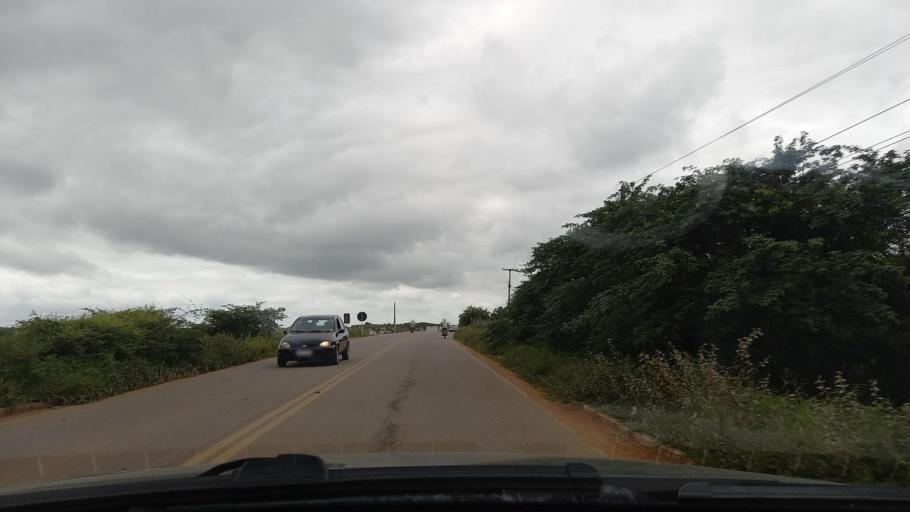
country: BR
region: Sergipe
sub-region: Caninde De Sao Francisco
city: Caninde de Sao Francisco
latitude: -9.6829
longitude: -37.7882
